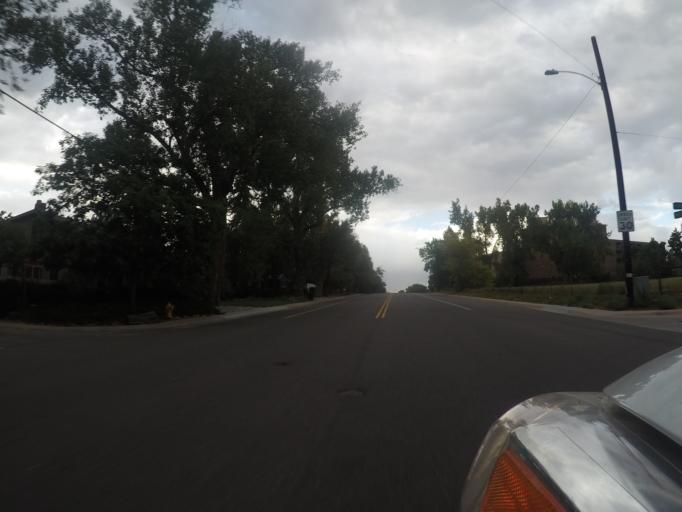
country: US
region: Colorado
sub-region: Arapahoe County
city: Littleton
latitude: 39.6096
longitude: -105.0069
